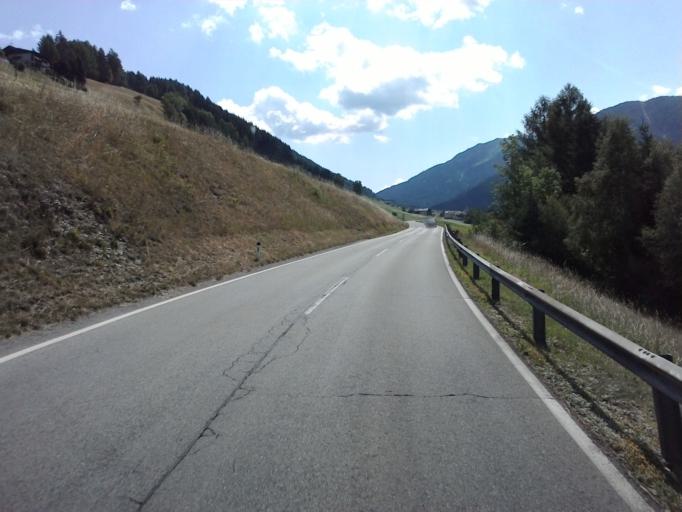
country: AT
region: Tyrol
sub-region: Politischer Bezirk Lienz
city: Strassen
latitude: 46.7362
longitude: 12.4768
